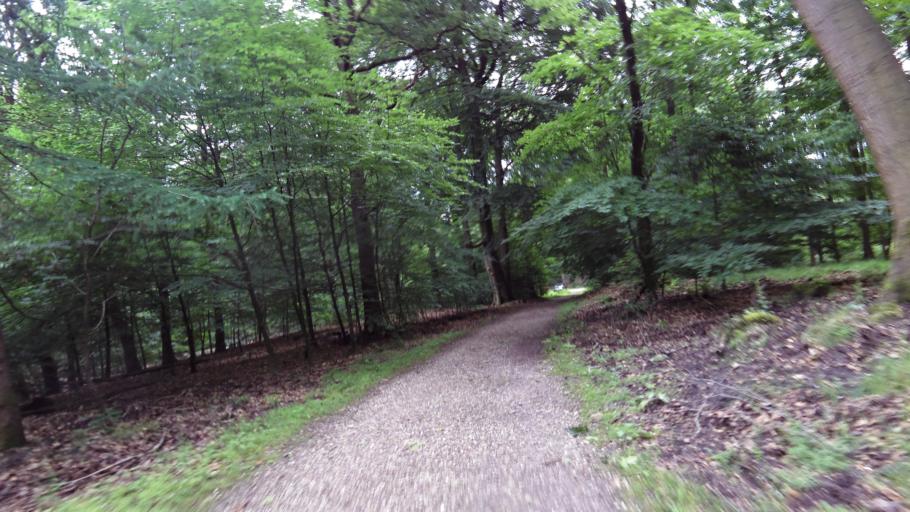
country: NL
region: Gelderland
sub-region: Gemeente Apeldoorn
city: Apeldoorn
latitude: 52.2213
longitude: 5.8923
